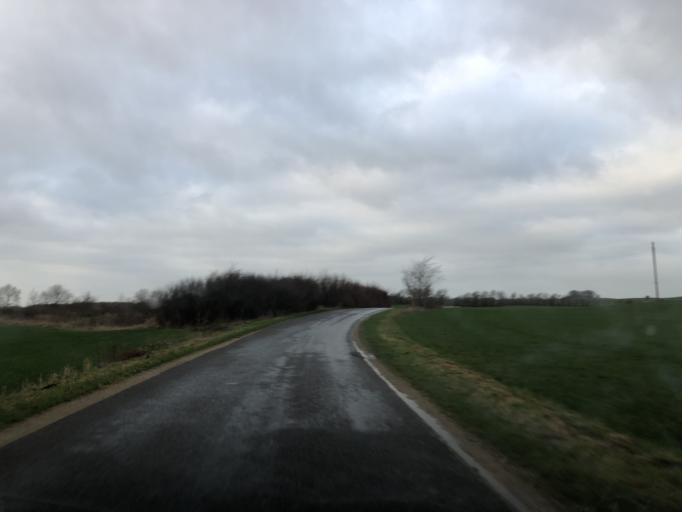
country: DK
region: North Denmark
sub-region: Vesthimmerland Kommune
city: Alestrup
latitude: 56.5940
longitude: 9.6051
